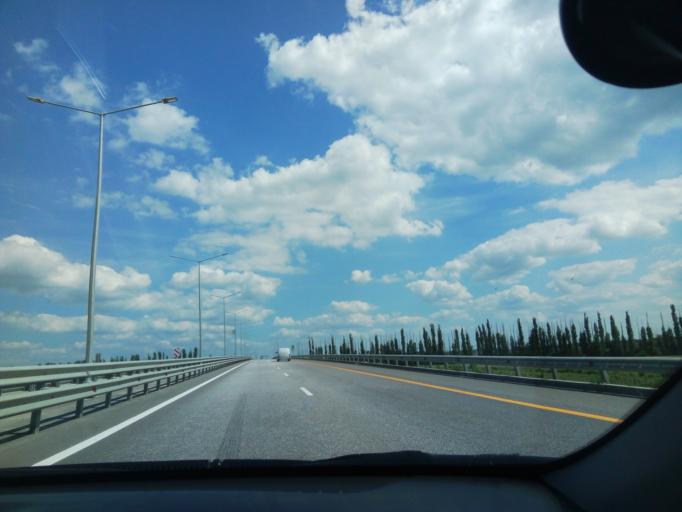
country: RU
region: Voronezj
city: Kashirskoye
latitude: 51.4838
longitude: 39.5400
